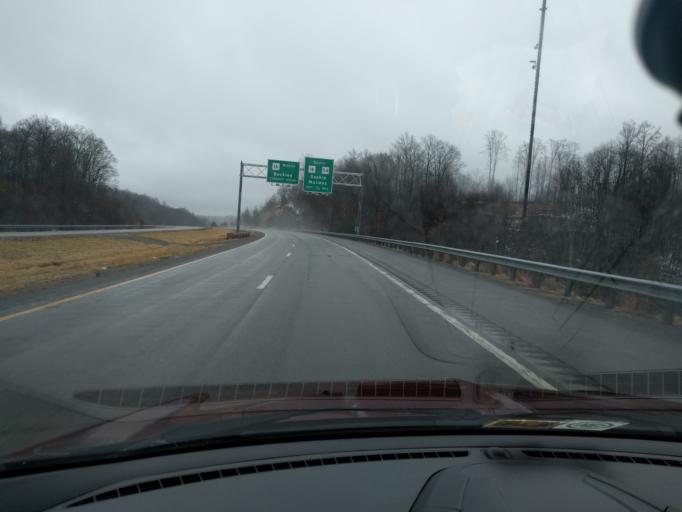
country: US
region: West Virginia
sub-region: Raleigh County
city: Sophia
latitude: 37.7127
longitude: -81.2655
